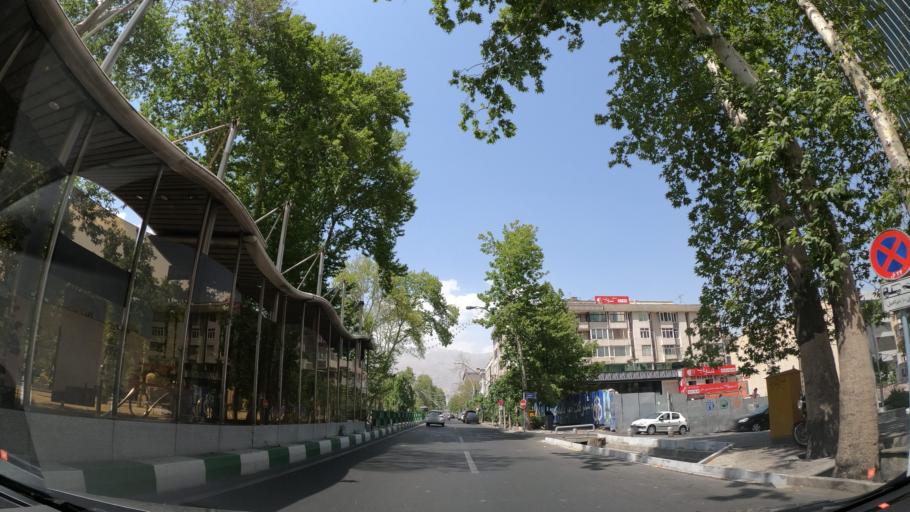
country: IR
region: Tehran
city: Tajrish
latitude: 35.7764
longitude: 51.4131
